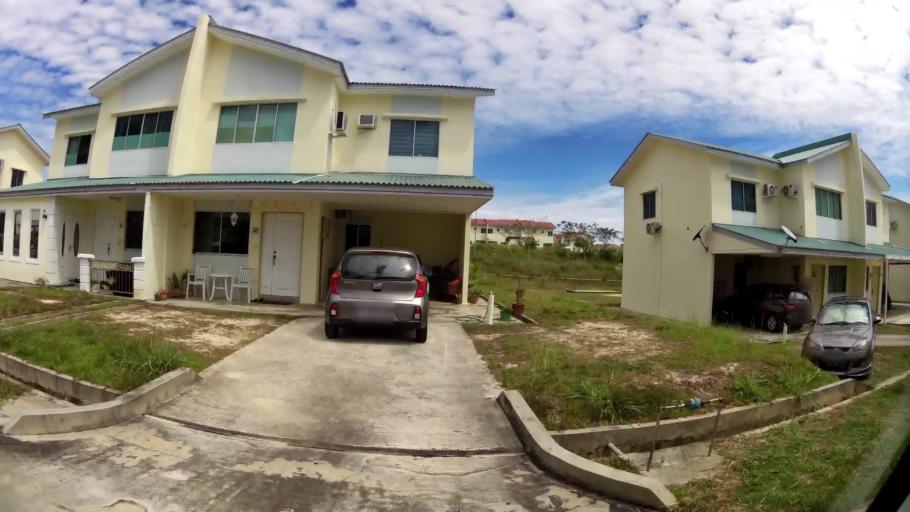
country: BN
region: Brunei and Muara
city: Bandar Seri Begawan
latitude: 4.9714
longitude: 115.0073
